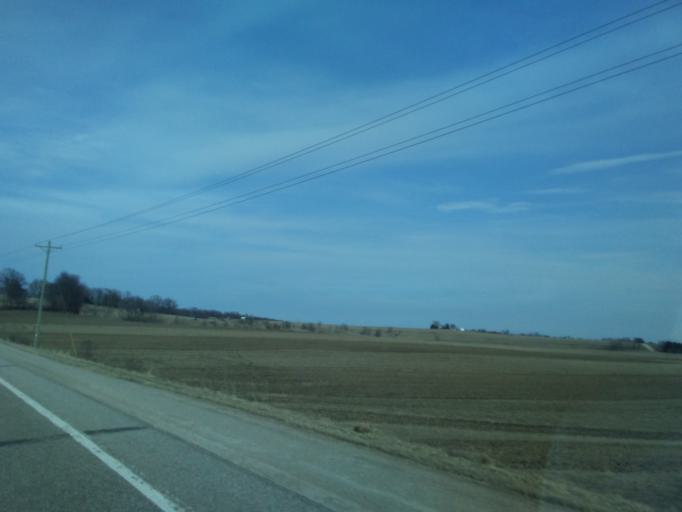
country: US
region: Wisconsin
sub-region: Grant County
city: Fennimore
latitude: 42.9830
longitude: -90.7229
